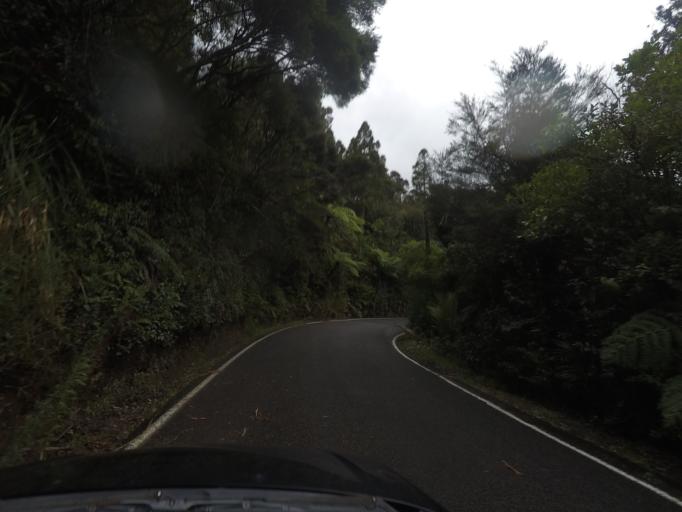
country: NZ
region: Auckland
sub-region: Auckland
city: Muriwai Beach
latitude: -36.9684
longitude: 174.4886
